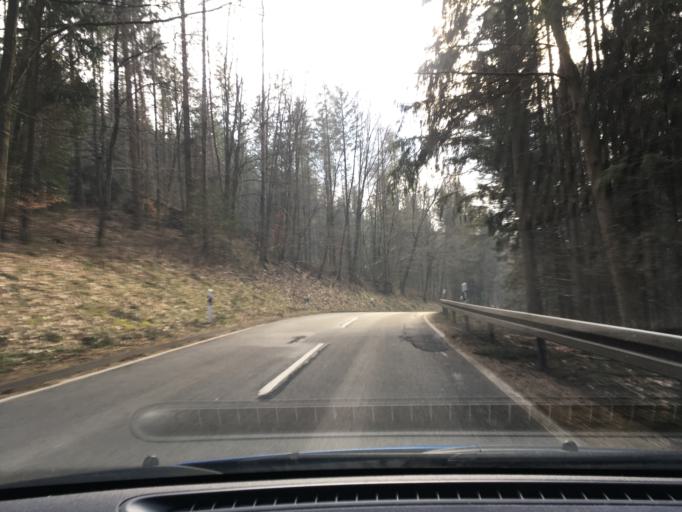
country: DE
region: Lower Saxony
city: Bodenfelde
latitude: 51.6258
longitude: 9.5900
